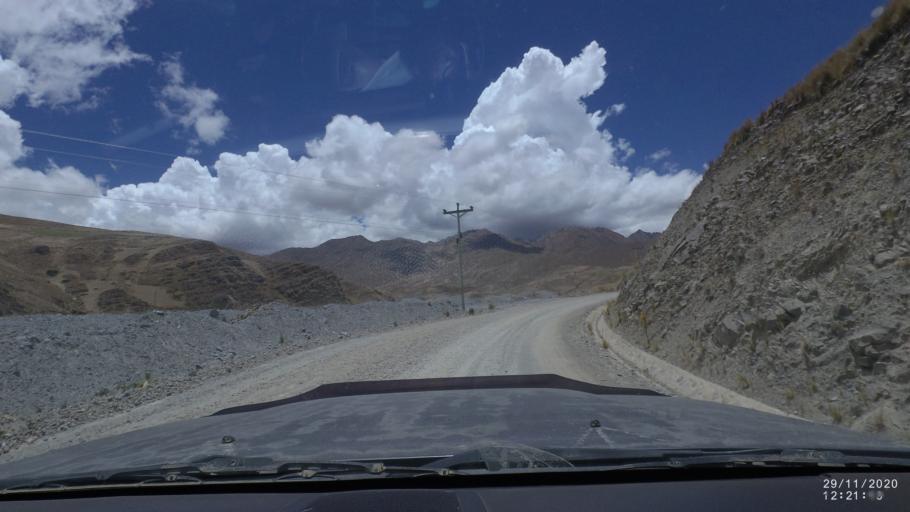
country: BO
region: Cochabamba
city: Cochabamba
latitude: -17.0984
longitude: -66.3208
